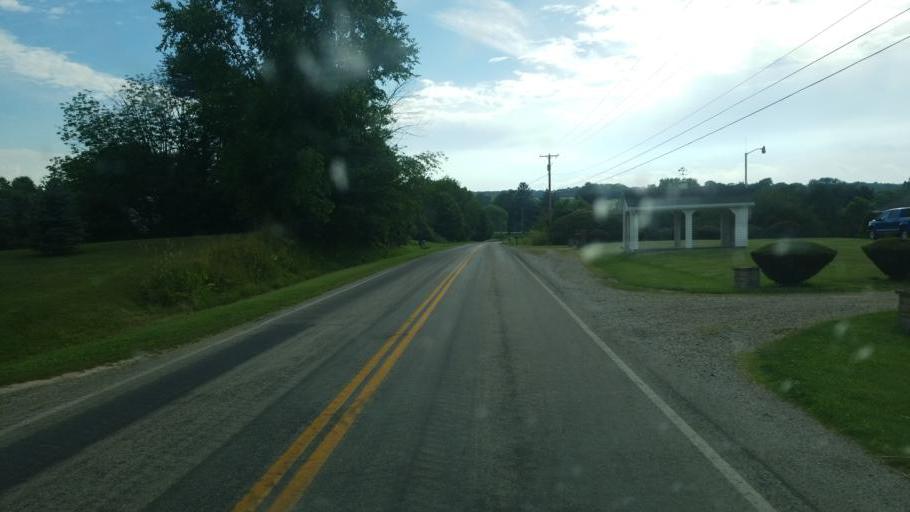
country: US
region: Ohio
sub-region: Ashland County
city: Ashland
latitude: 40.7724
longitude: -82.2819
